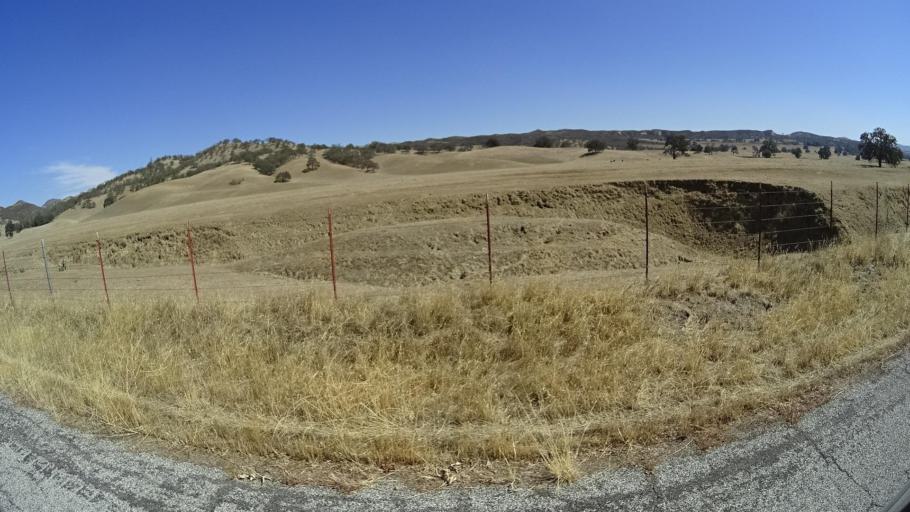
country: US
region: California
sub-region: San Luis Obispo County
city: San Miguel
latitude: 36.0395
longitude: -120.6654
